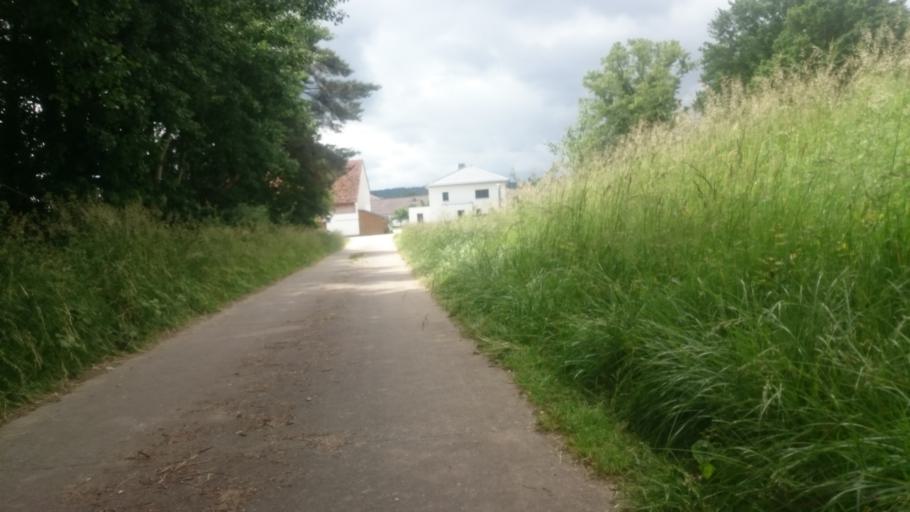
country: DE
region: Bavaria
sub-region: Upper Palatinate
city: Freystadt
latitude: 49.1509
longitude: 11.3215
